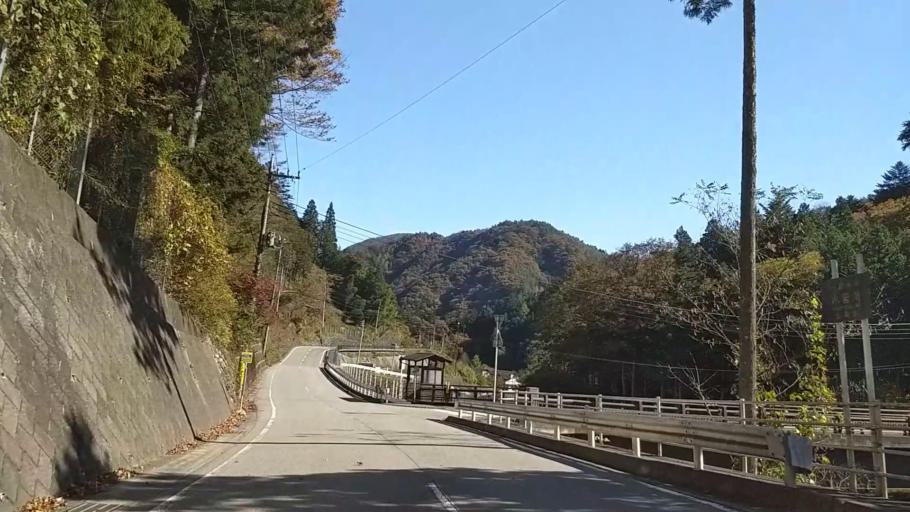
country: JP
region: Yamanashi
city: Otsuki
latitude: 35.7588
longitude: 138.9473
